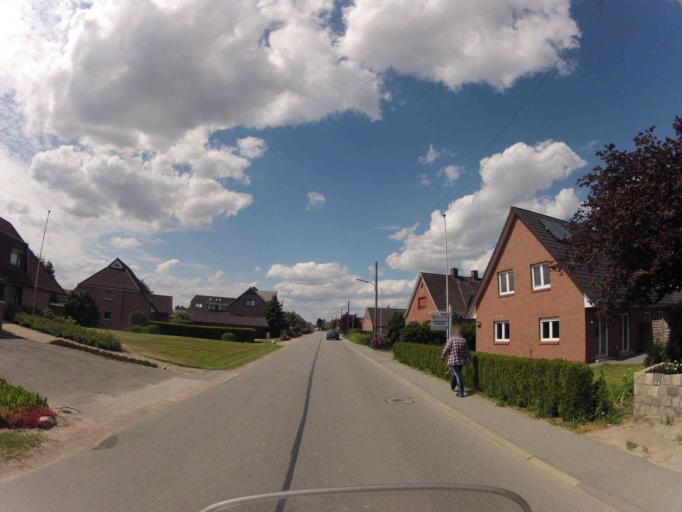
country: DE
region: Hamburg
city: Bergedorf
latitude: 53.4323
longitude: 10.1939
